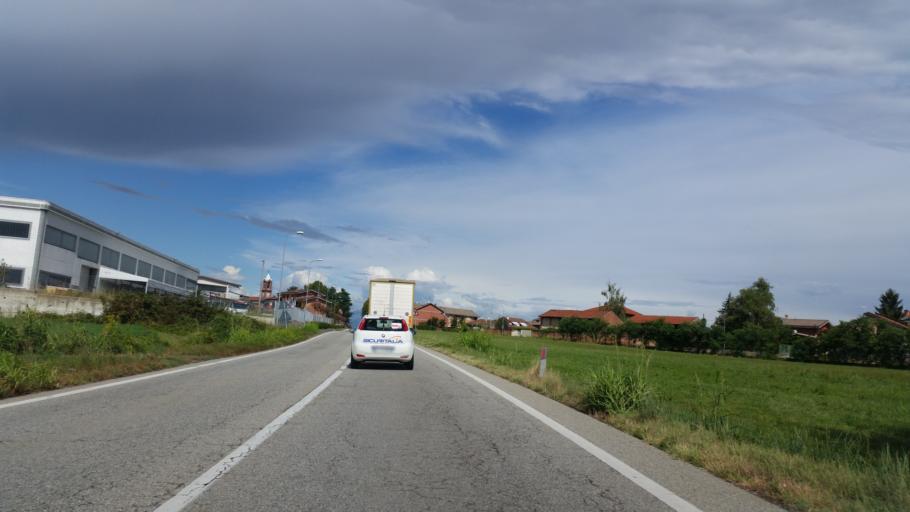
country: IT
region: Piedmont
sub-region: Provincia di Torino
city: Marocchi
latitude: 44.9371
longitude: 7.8266
